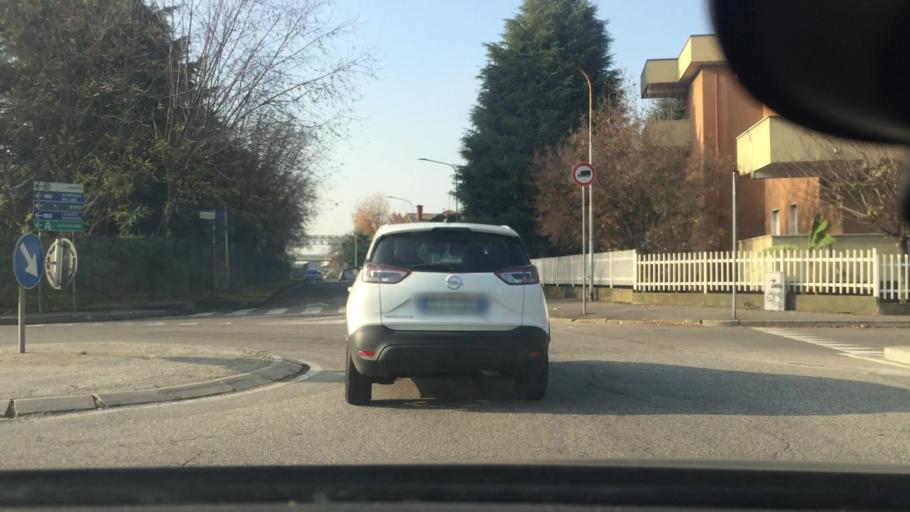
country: IT
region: Lombardy
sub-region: Citta metropolitana di Milano
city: Passirana
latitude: 45.5461
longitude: 9.0442
